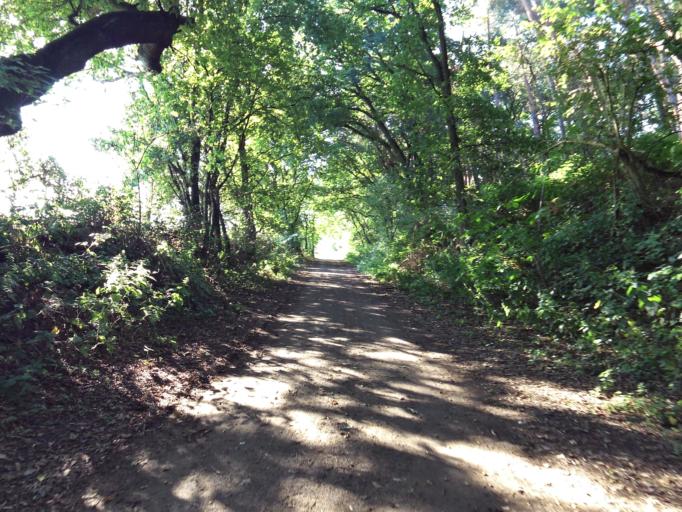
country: DE
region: North Rhine-Westphalia
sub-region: Regierungsbezirk Koln
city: Alsdorf
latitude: 50.8545
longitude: 6.1650
